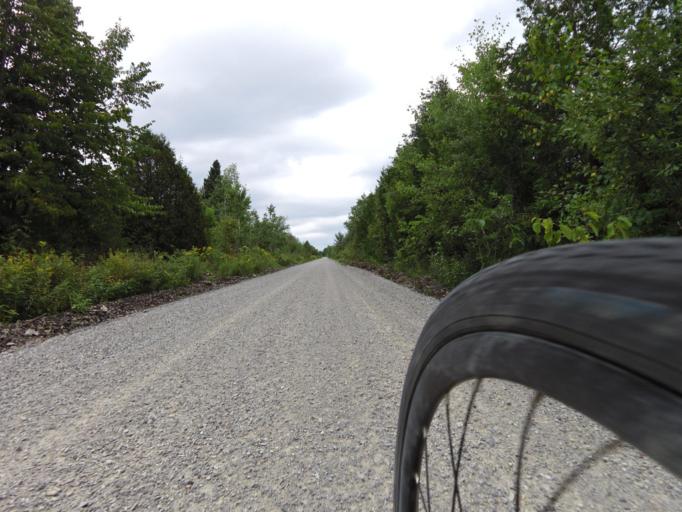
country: CA
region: Ontario
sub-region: Lanark County
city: Smiths Falls
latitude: 44.9473
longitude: -76.0426
